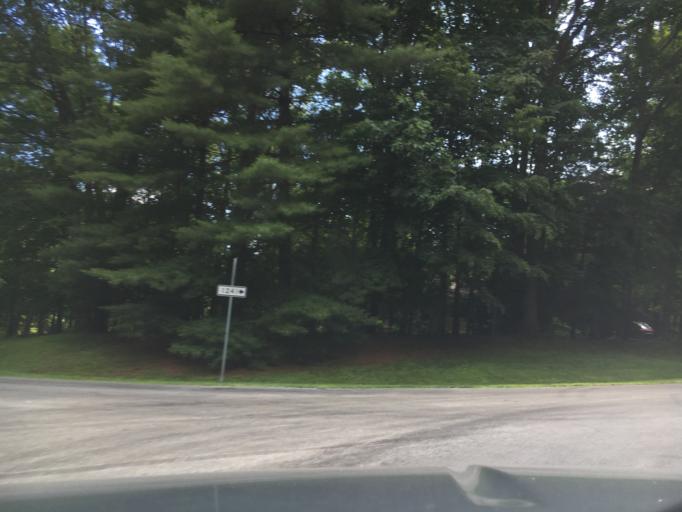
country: US
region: Virginia
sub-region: Bedford County
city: Forest
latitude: 37.3875
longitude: -79.2528
